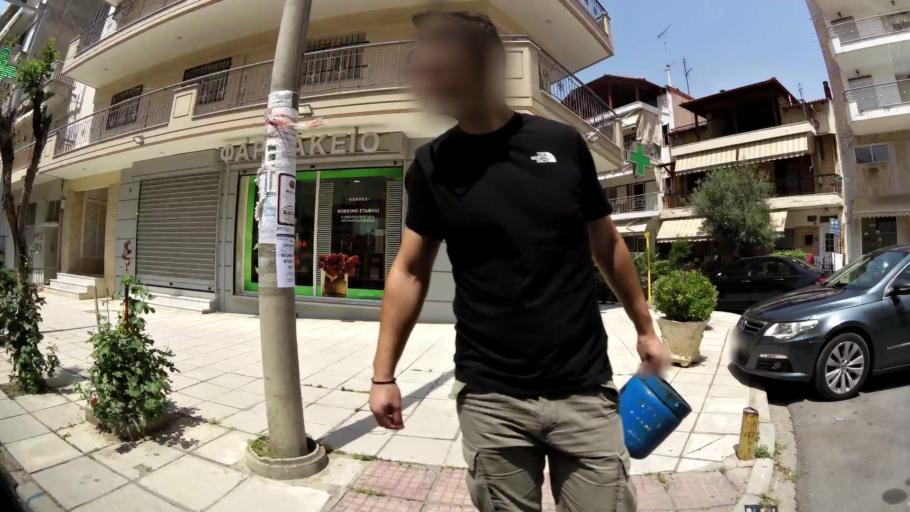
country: GR
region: Central Macedonia
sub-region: Nomos Thessalonikis
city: Evosmos
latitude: 40.6703
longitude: 22.8983
